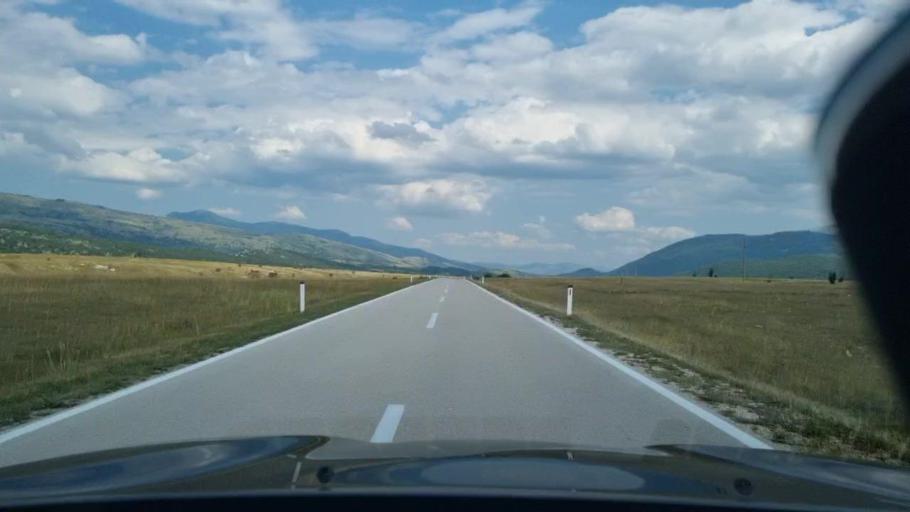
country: BA
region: Federation of Bosnia and Herzegovina
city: Bosansko Grahovo
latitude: 44.1569
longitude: 16.4293
